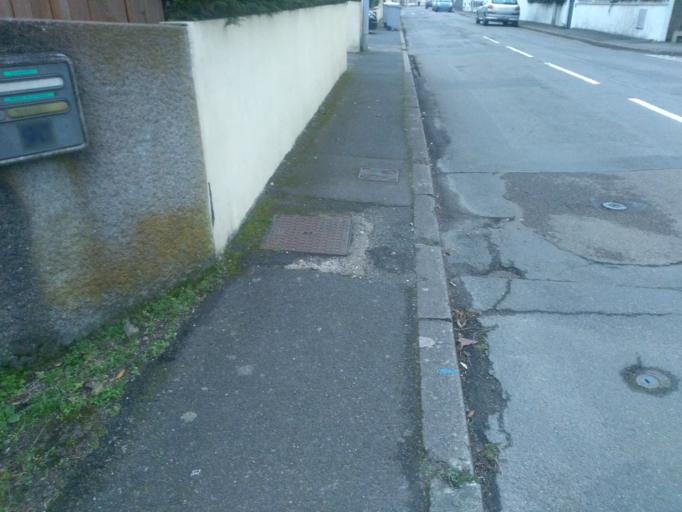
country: FR
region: Pays de la Loire
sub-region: Departement de la Loire-Atlantique
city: Saint-Sebastien-sur-Loire
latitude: 47.1906
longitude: -1.5044
